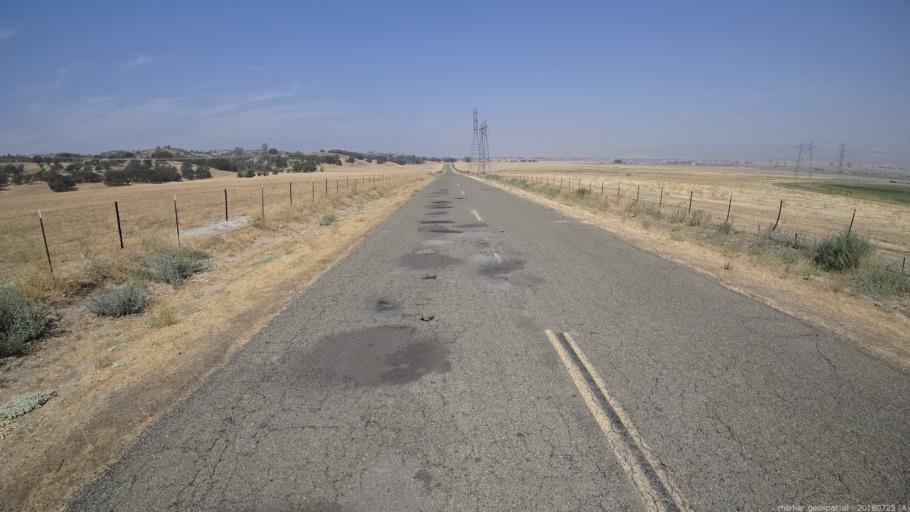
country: US
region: California
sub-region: San Luis Obispo County
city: Shandon
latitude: 35.8167
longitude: -120.3781
